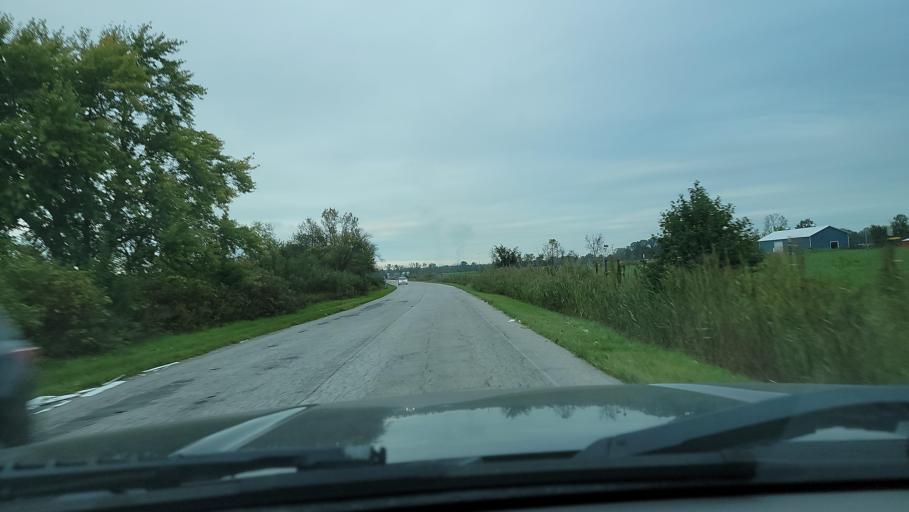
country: US
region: Indiana
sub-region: Porter County
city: South Haven
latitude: 41.5587
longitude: -87.1532
